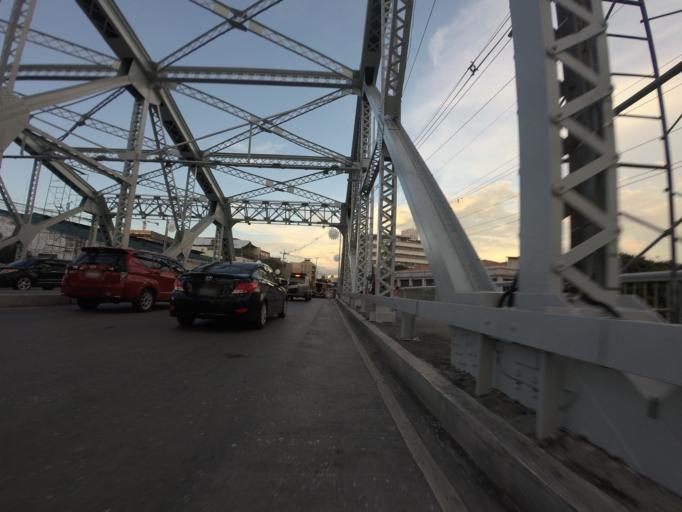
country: PH
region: Metro Manila
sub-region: City of Manila
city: Quiapo
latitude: 14.5916
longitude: 120.9867
